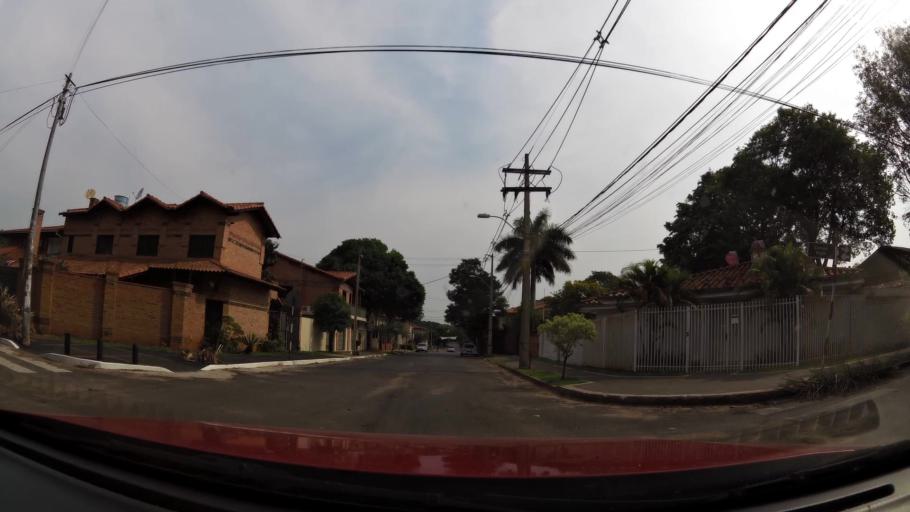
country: PY
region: Central
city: Fernando de la Mora
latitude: -25.2995
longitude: -57.5595
